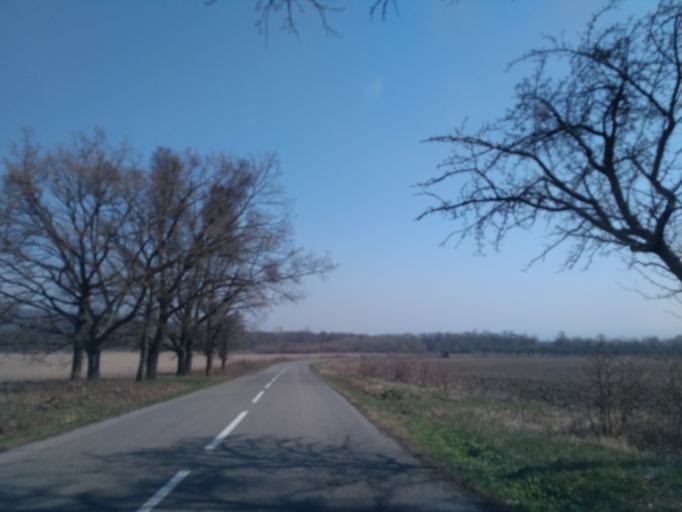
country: SK
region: Kosicky
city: Secovce
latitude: 48.7353
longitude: 21.6026
